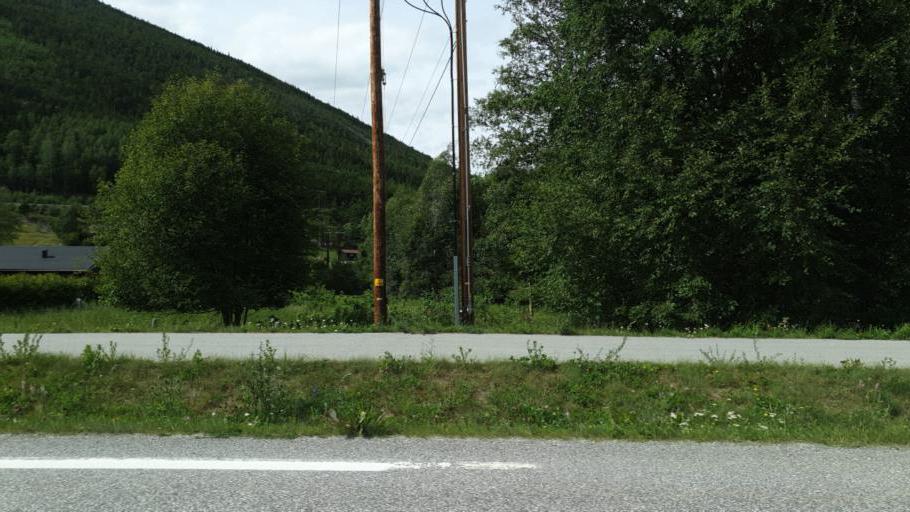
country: NO
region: Oppland
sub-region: Sel
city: Otta
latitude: 61.8472
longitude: 9.4183
